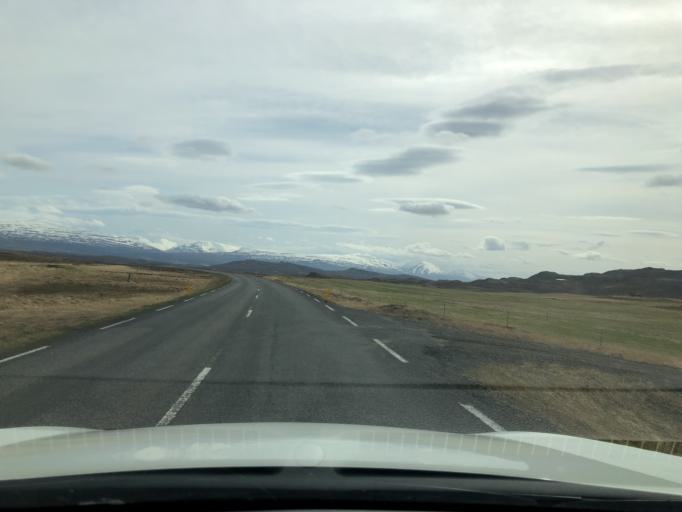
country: IS
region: East
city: Egilsstadir
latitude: 65.3645
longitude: -14.5272
